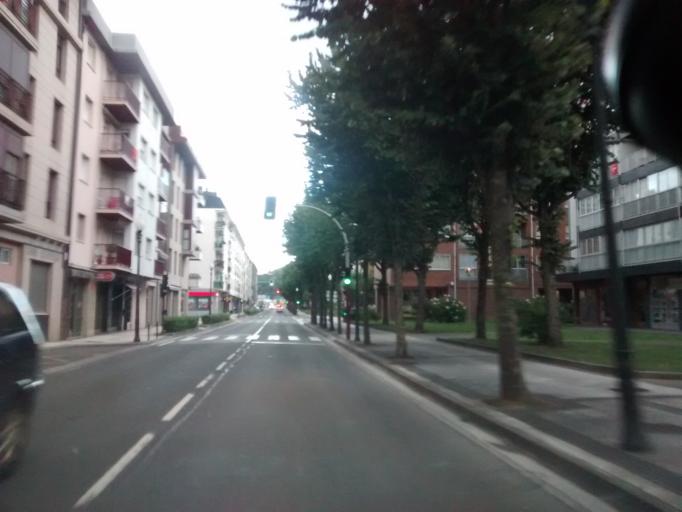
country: ES
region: Basque Country
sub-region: Provincia de Guipuzcoa
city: Zumaia
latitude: 43.2945
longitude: -2.2569
